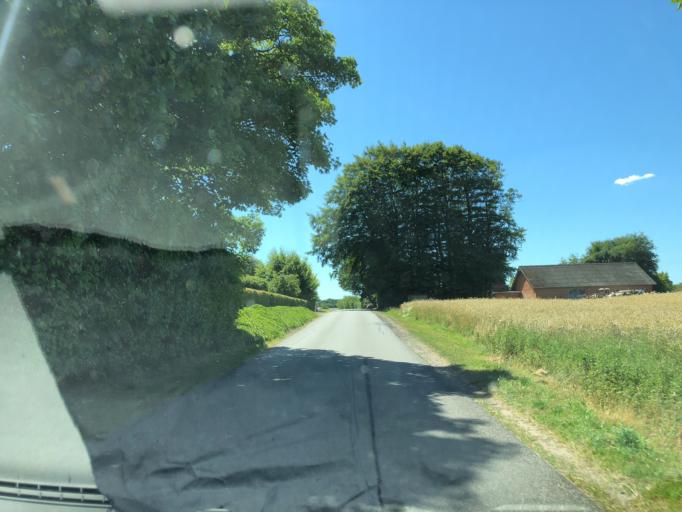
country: DK
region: Central Jutland
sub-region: Viborg Kommune
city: Viborg
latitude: 56.5107
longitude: 9.5077
